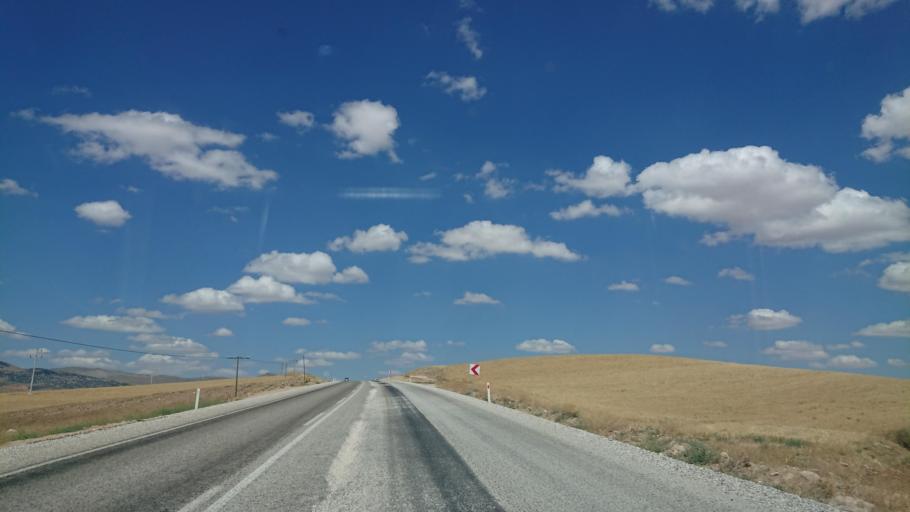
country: TR
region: Ankara
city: Evren
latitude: 39.1118
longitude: 33.9359
